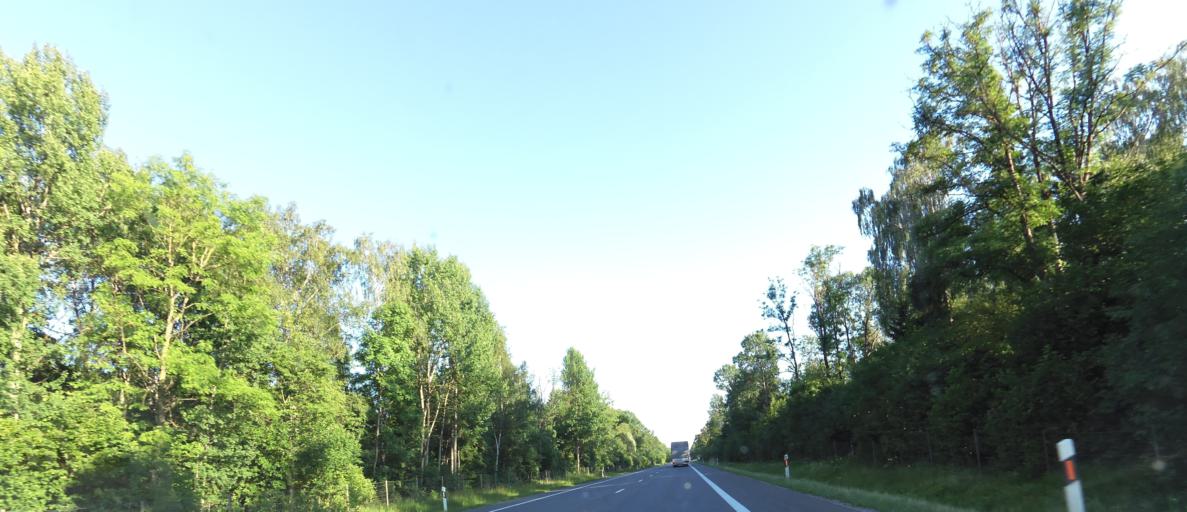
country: LT
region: Panevezys
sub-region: Panevezys City
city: Panevezys
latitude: 55.8191
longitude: 24.3674
